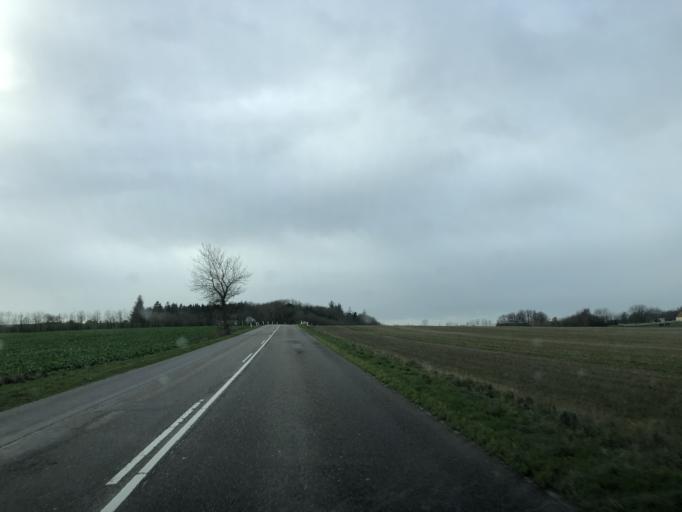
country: DK
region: North Denmark
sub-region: Rebild Kommune
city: Stovring
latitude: 56.8825
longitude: 9.7760
